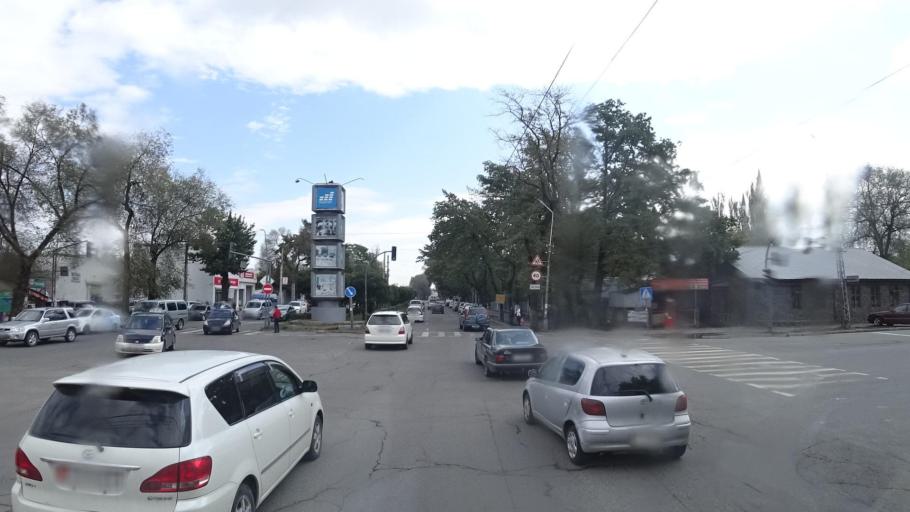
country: KG
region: Chuy
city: Bishkek
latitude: 42.8850
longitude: 74.6163
